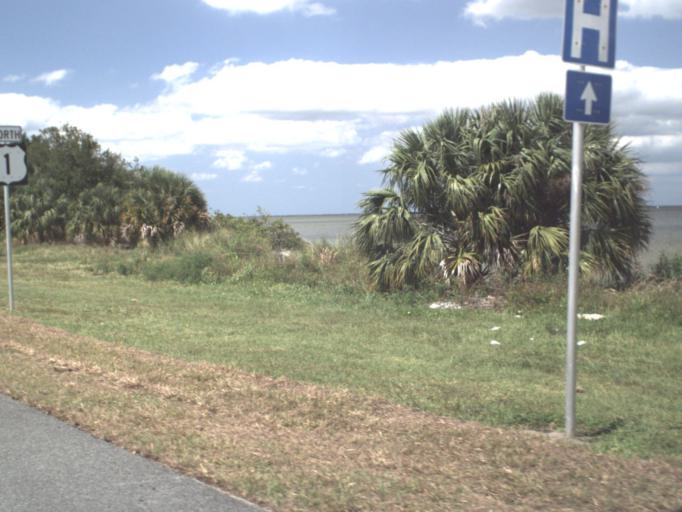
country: US
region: Florida
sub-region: Brevard County
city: Titusville
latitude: 28.5587
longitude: -80.7982
